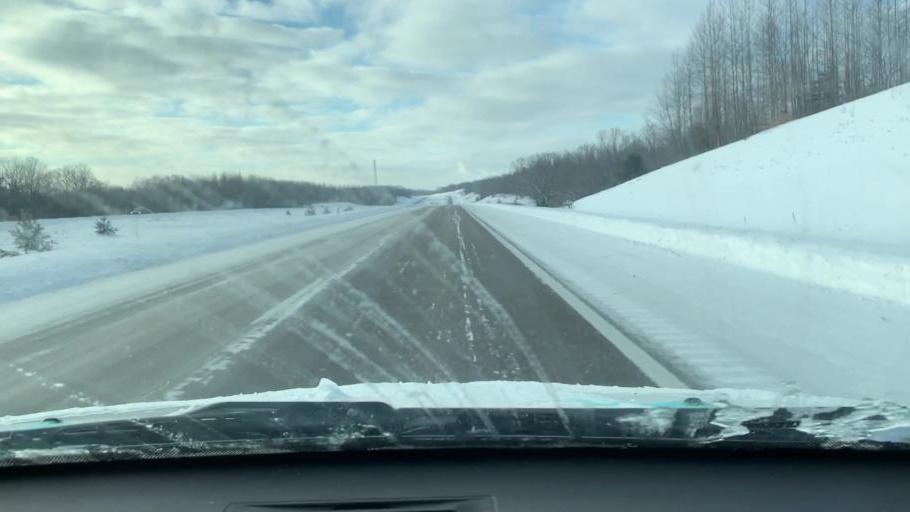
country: US
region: Michigan
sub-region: Wexford County
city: Manton
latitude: 44.3486
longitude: -85.4047
